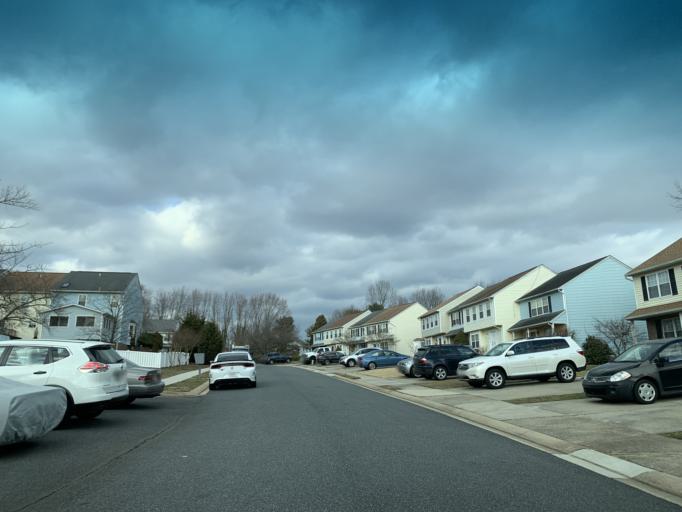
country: US
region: Maryland
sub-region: Harford County
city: Bel Air South
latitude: 39.5309
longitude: -76.3008
